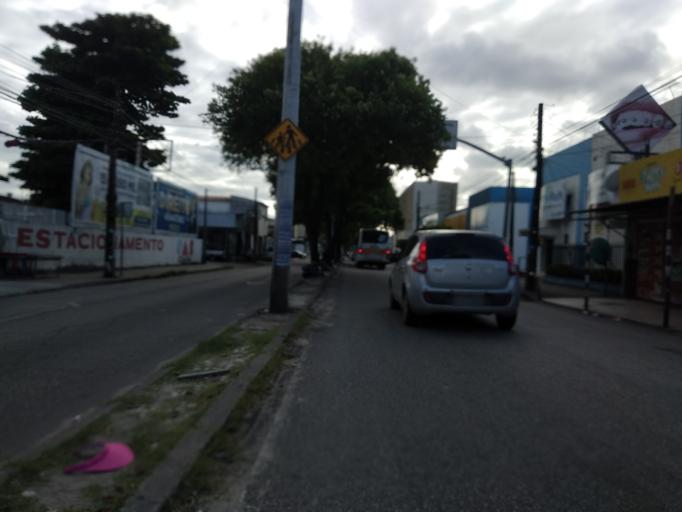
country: BR
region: Ceara
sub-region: Fortaleza
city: Fortaleza
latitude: -3.7298
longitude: -38.5363
